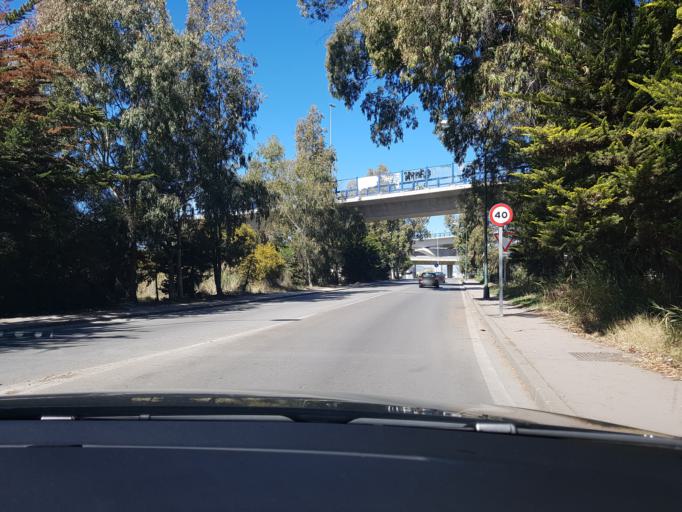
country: ES
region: Andalusia
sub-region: Provincia de Malaga
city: Torremolinos
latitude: 36.6689
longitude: -4.4651
